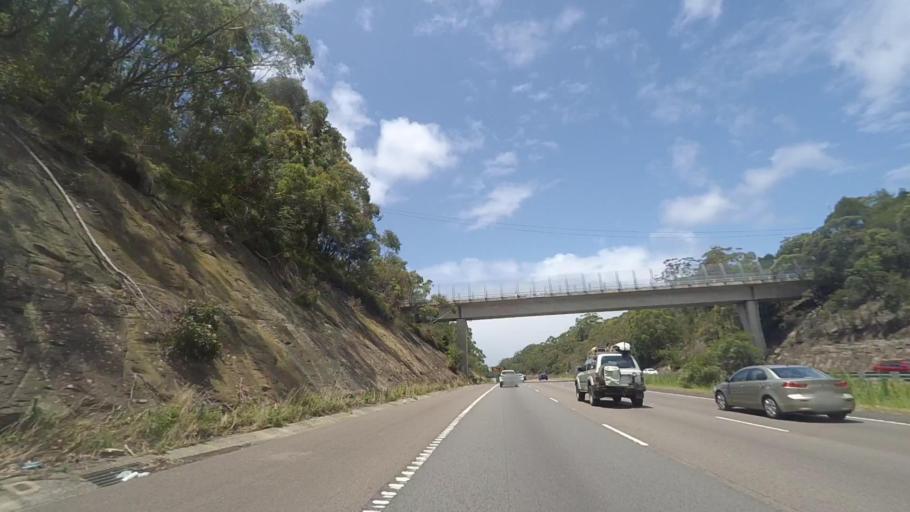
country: AU
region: New South Wales
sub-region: Gosford Shire
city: Lisarow
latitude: -33.3596
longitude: 151.3381
